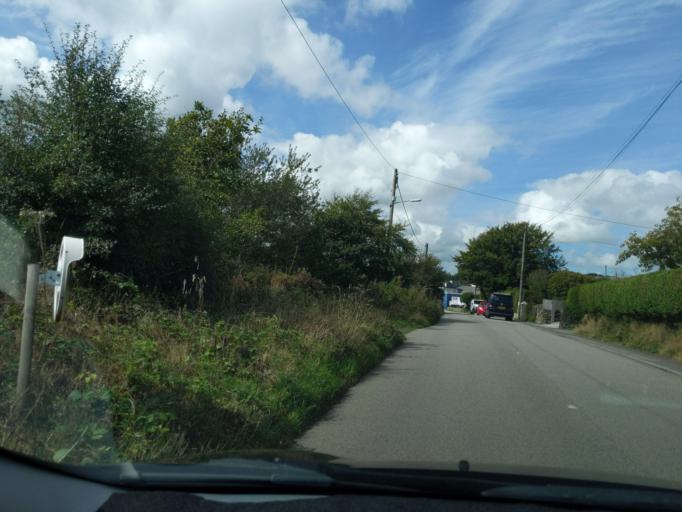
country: GB
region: England
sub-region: Cornwall
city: Callington
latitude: 50.5181
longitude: -4.3135
